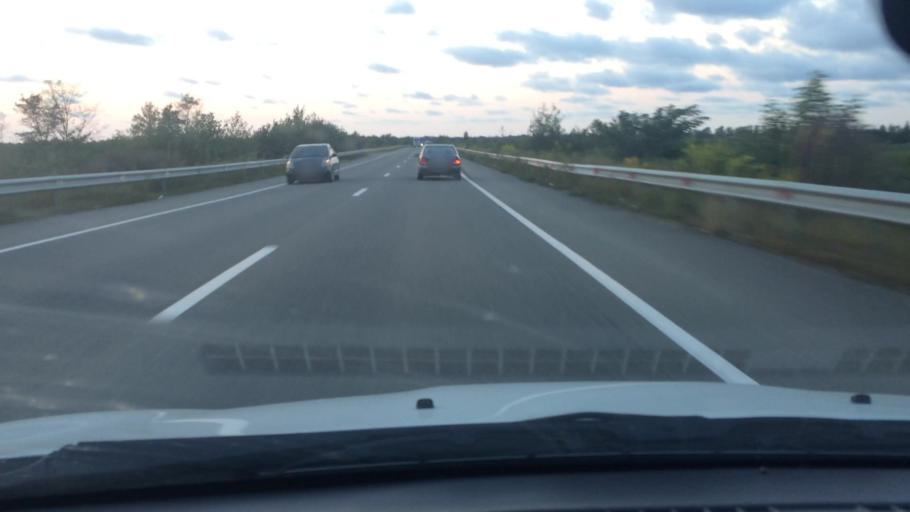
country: GE
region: Ajaria
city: Ochkhamuri
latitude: 41.9051
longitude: 41.7891
